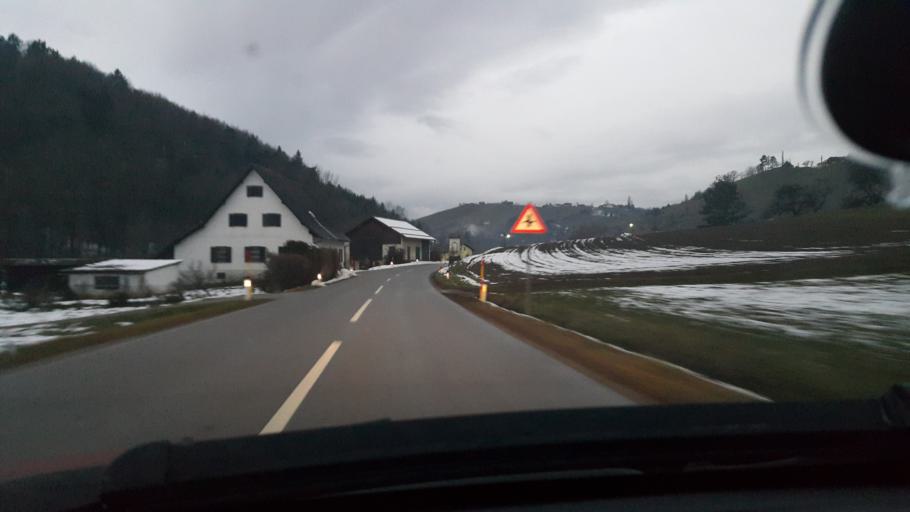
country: AT
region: Styria
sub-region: Politischer Bezirk Leibnitz
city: Sulztal an der Weinstrasse
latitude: 46.6456
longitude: 15.5541
